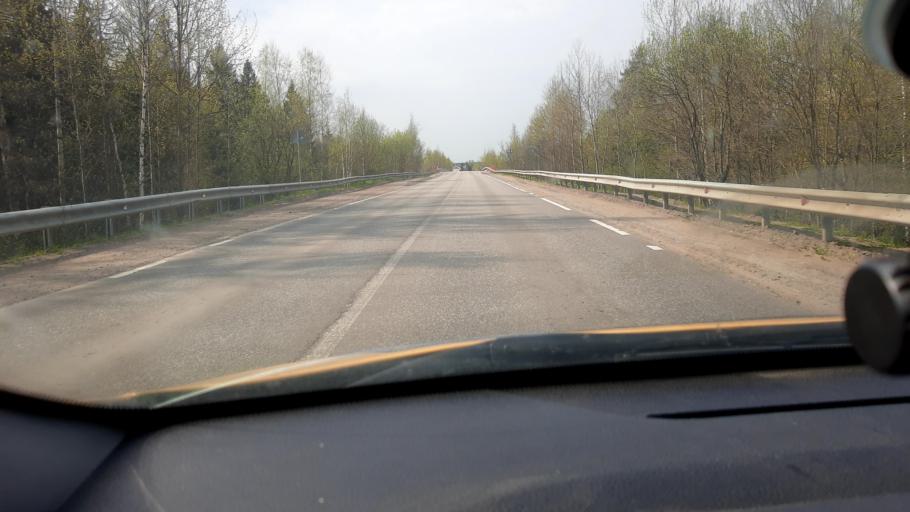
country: RU
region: Moskovskaya
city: Rumyantsevo
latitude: 55.9172
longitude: 36.6016
